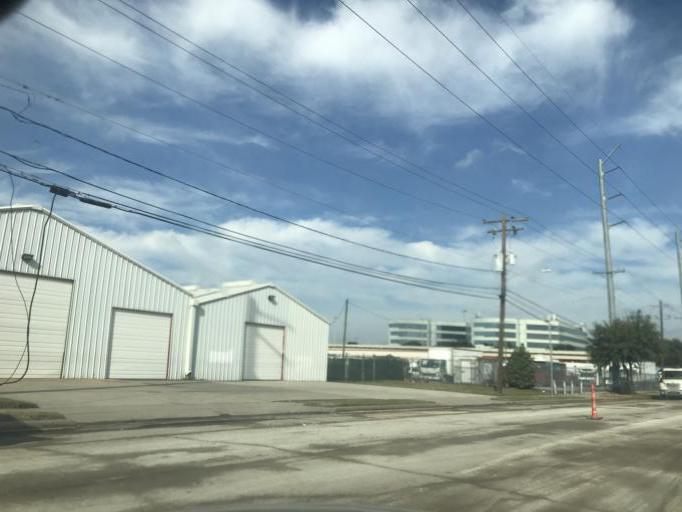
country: US
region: Texas
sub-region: Harris County
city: Bellaire
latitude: 29.7227
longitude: -95.4806
